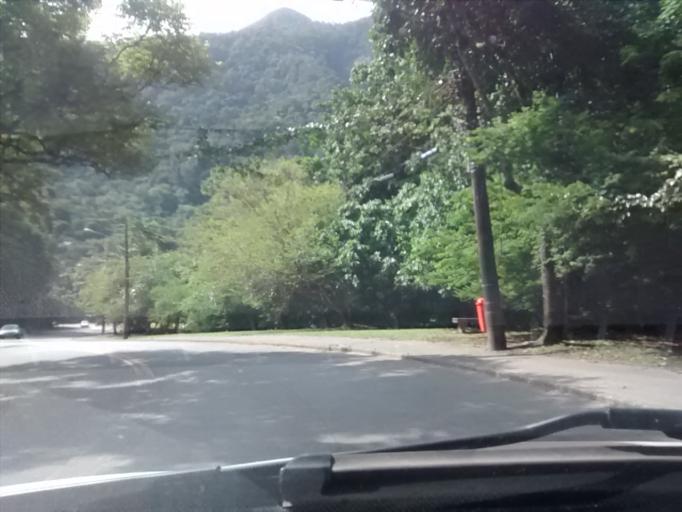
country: BR
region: Rio de Janeiro
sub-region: Rio De Janeiro
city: Rio de Janeiro
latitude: -22.9578
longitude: -43.2643
